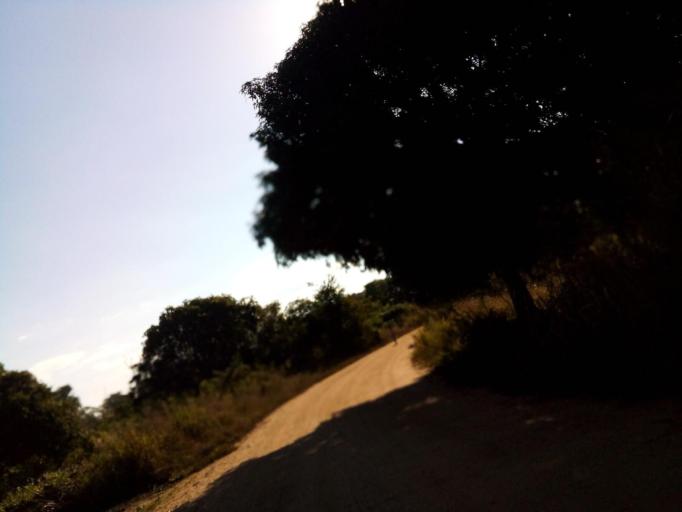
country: MZ
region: Zambezia
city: Quelimane
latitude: -17.4891
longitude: 36.5617
